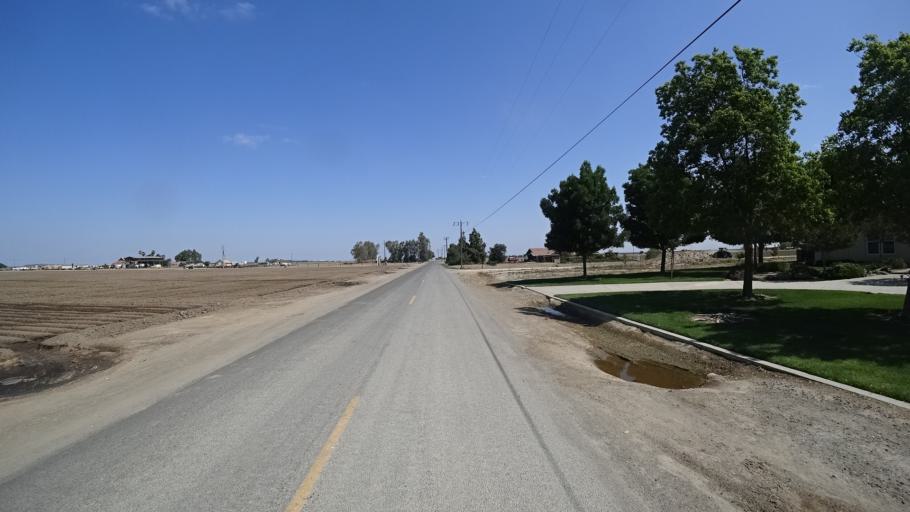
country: US
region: California
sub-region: Kings County
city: Home Garden
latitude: 36.2222
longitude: -119.6279
